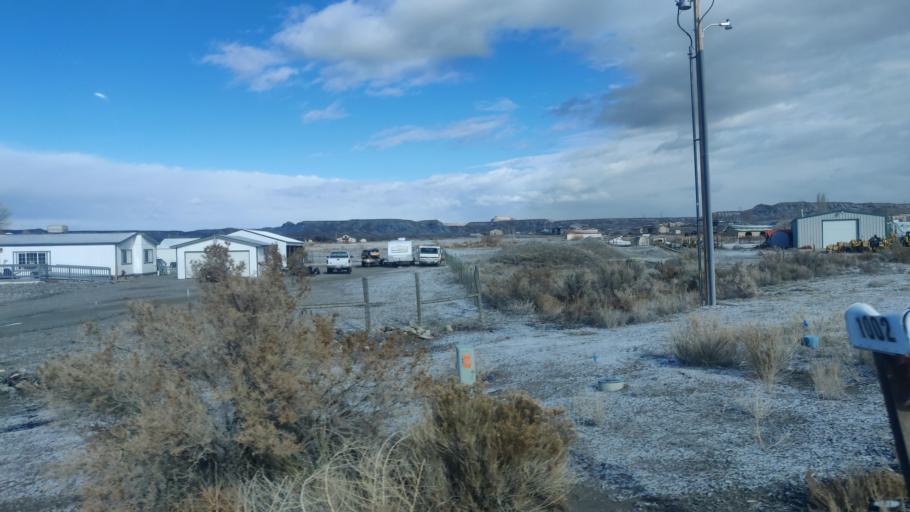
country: US
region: Colorado
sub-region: Mesa County
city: Clifton
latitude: 38.9906
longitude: -108.4274
